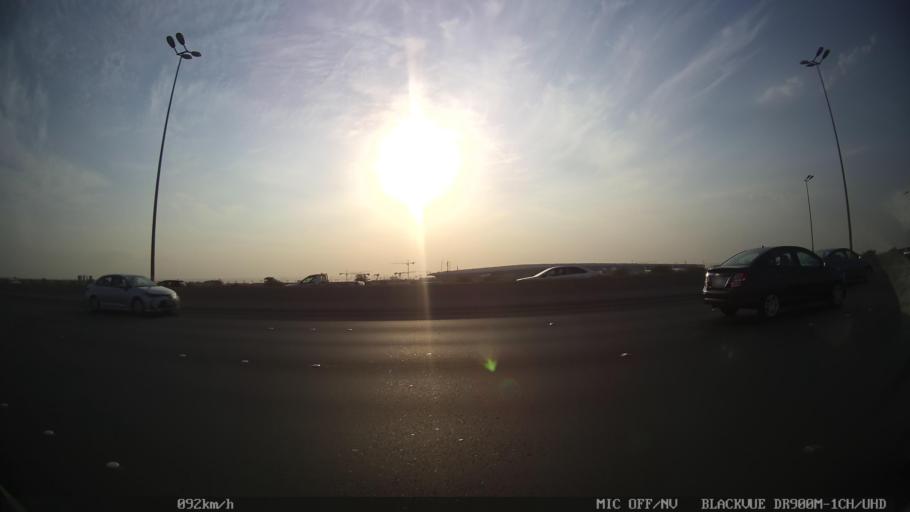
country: KW
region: Al Farwaniyah
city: Janub as Surrah
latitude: 29.2168
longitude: 48.0011
